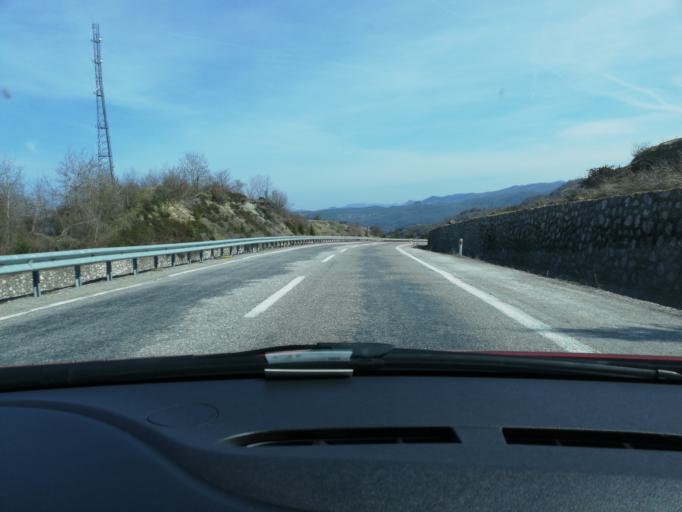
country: TR
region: Bartin
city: Amasra
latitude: 41.7304
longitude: 32.4107
